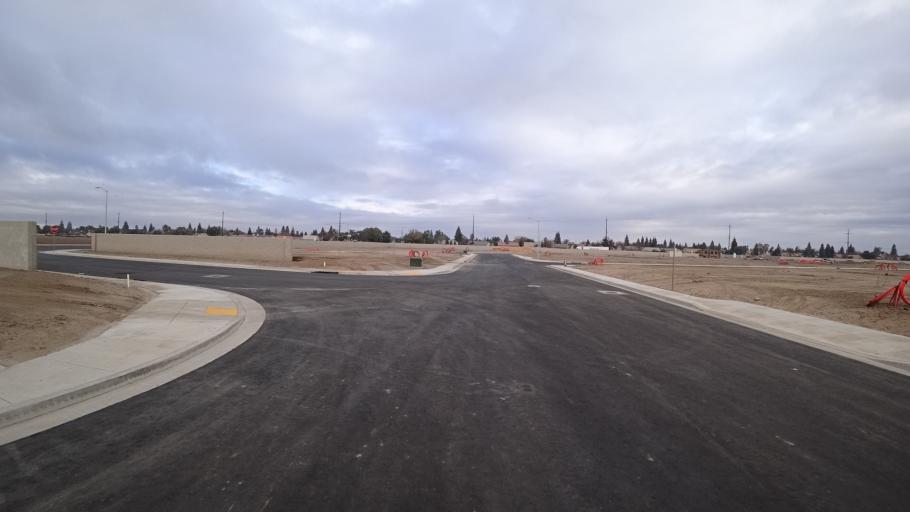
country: US
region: California
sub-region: Kern County
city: Greenfield
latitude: 35.2942
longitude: -119.0827
